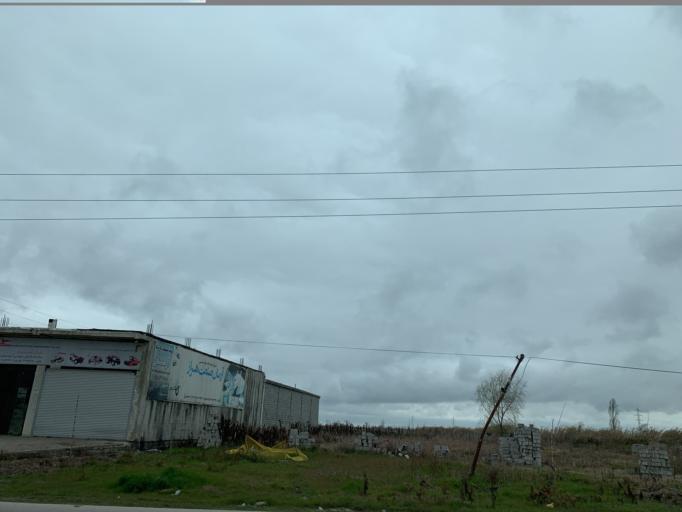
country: IR
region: Mazandaran
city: Babol
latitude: 36.5124
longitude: 52.5585
